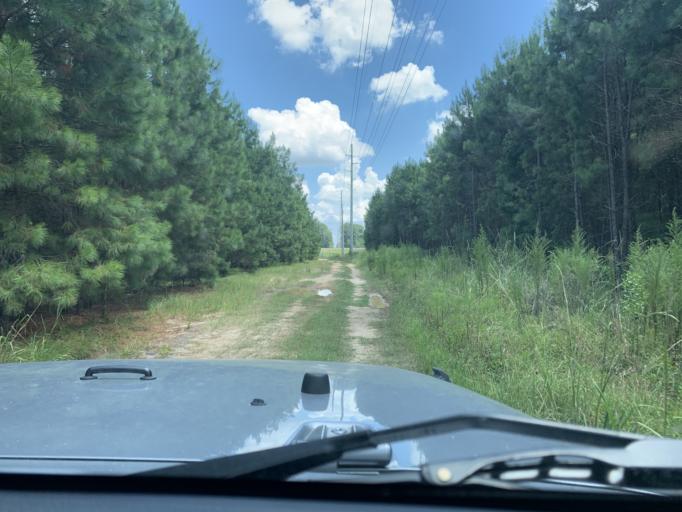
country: US
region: Georgia
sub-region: Chatham County
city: Pooler
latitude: 32.1210
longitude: -81.2713
